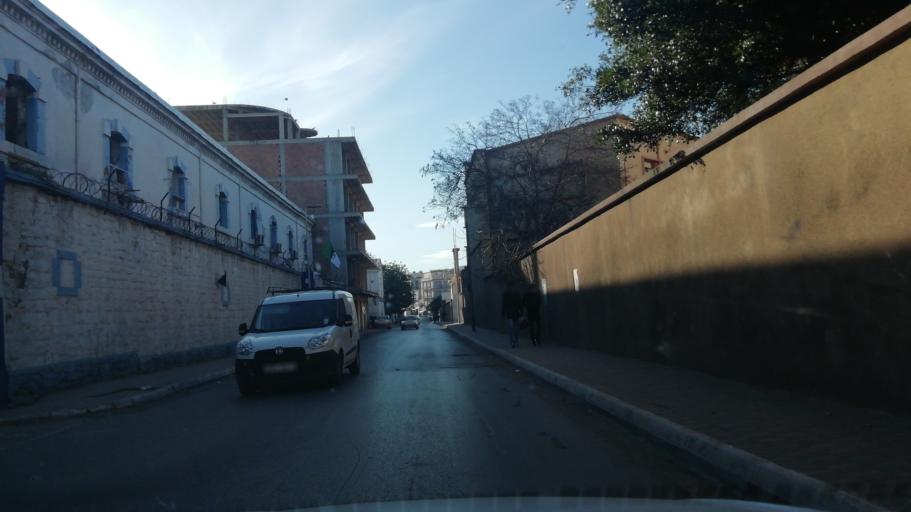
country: DZ
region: Oran
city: Oran
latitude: 35.6932
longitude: -0.6426
